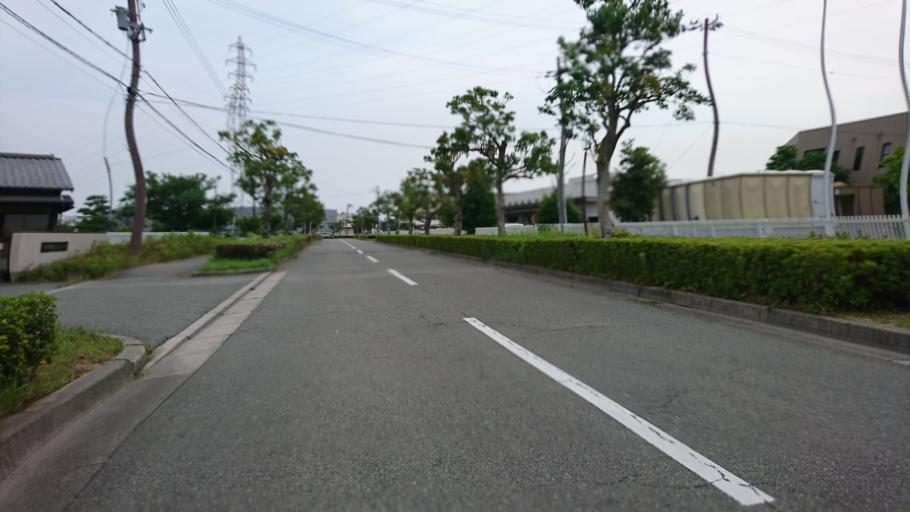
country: JP
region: Hyogo
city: Kakogawacho-honmachi
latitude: 34.7382
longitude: 134.8854
